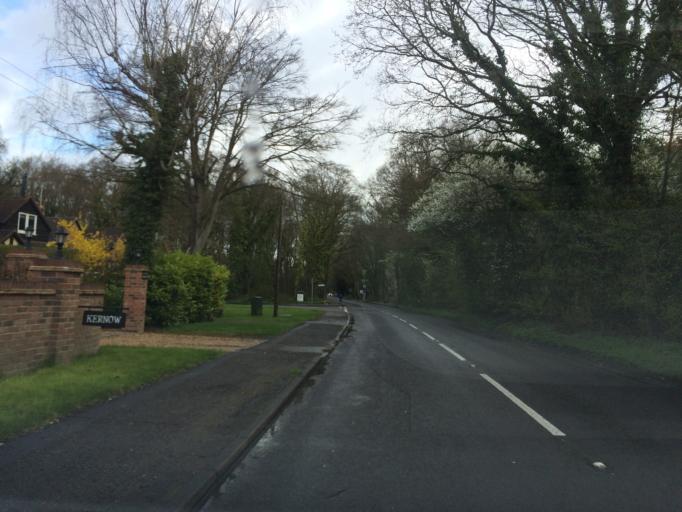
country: GB
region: England
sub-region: Surrey
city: Chobham
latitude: 51.3378
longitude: -0.6095
